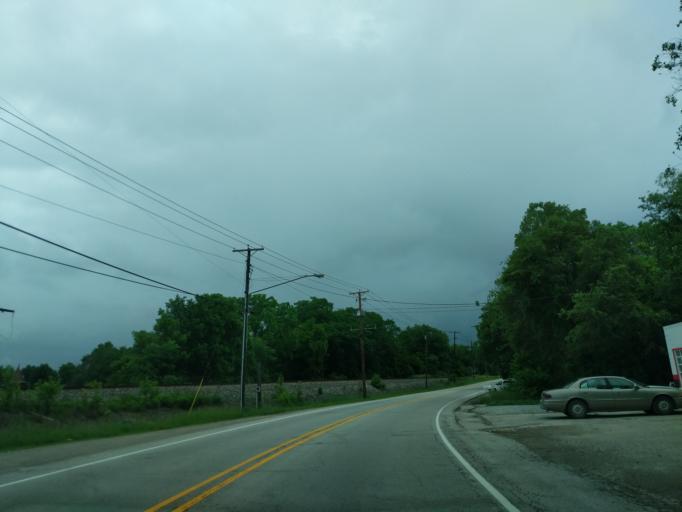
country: US
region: Indiana
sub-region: Delaware County
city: Daleville
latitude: 40.1220
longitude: -85.5585
